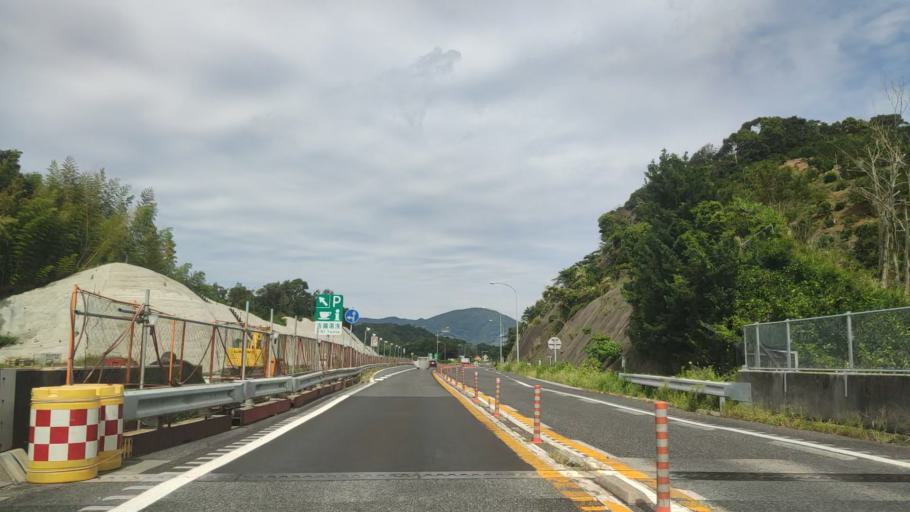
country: JP
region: Wakayama
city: Kainan
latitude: 34.0343
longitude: 135.2009
